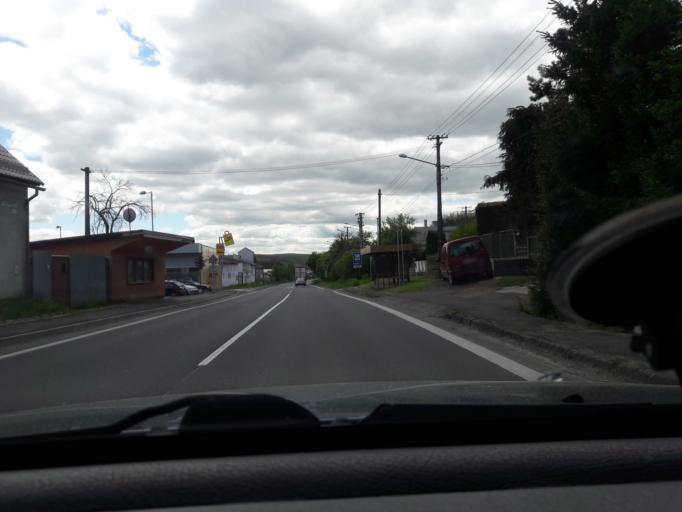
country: SK
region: Banskobystricky
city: Krupina
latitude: 48.3470
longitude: 19.0664
